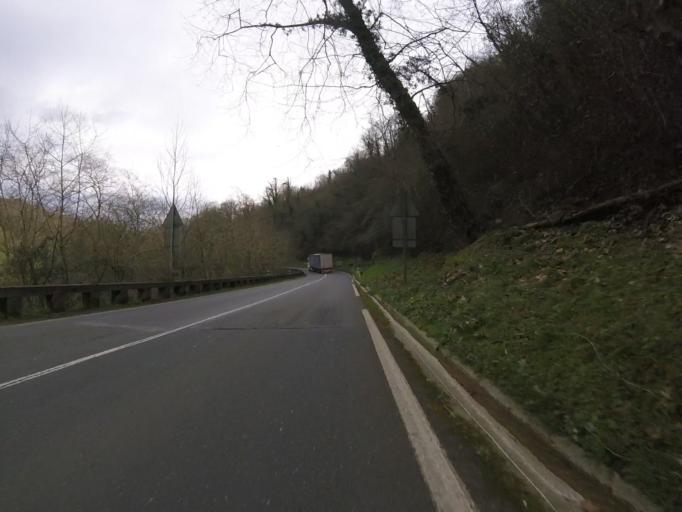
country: ES
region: Basque Country
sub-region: Provincia de Guipuzcoa
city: Cestona
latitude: 43.2525
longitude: -2.2521
